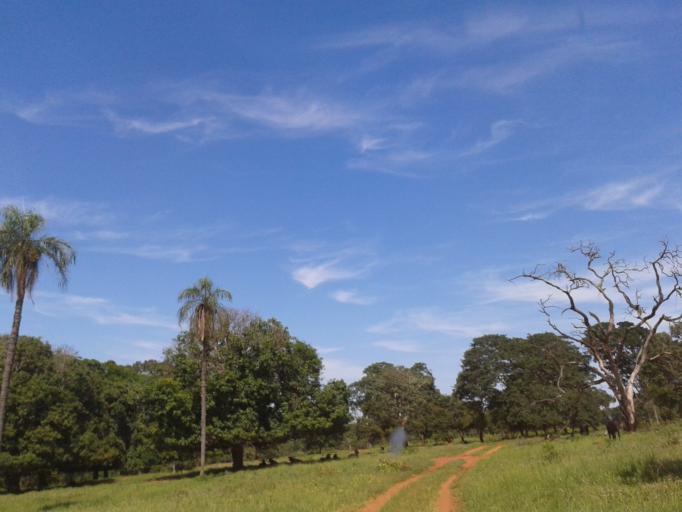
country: BR
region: Minas Gerais
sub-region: Santa Vitoria
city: Santa Vitoria
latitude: -19.1683
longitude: -50.5228
